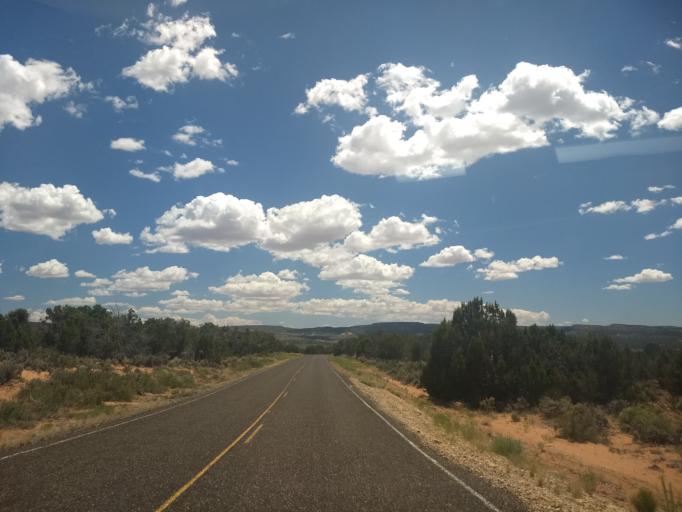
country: US
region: Utah
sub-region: Kane County
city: Kanab
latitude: 37.1821
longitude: -112.6554
